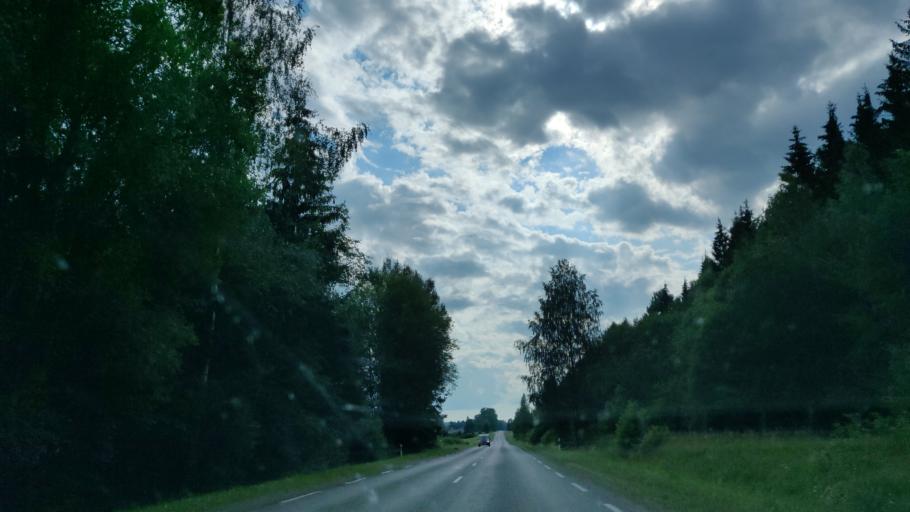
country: LT
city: Rietavas
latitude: 55.7056
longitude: 21.8351
